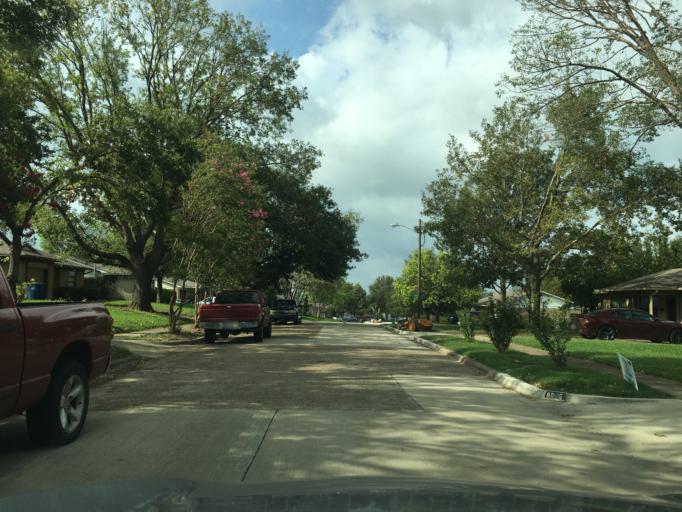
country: US
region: Texas
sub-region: Dallas County
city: Richardson
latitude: 32.8972
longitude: -96.7533
